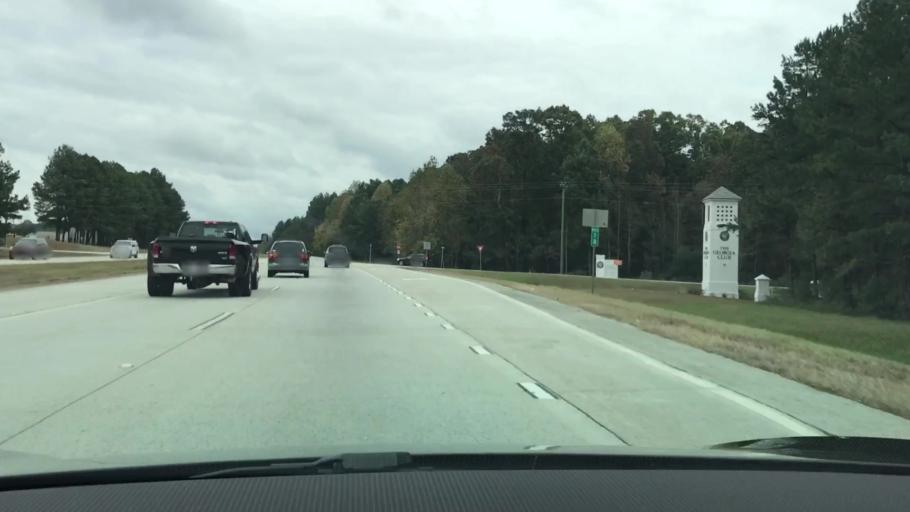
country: US
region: Georgia
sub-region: Barrow County
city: Statham
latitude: 33.9471
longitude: -83.5832
